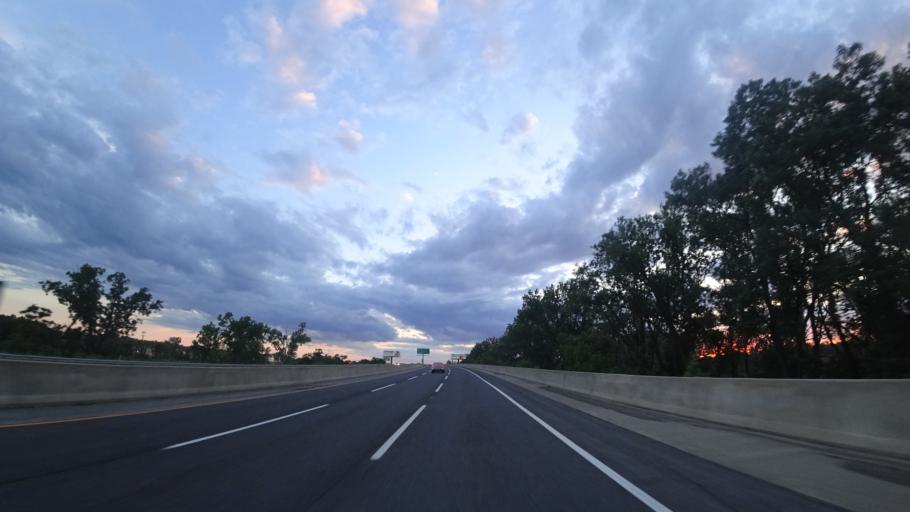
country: US
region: Indiana
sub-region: Lake County
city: Gary
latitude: 41.6097
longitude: -87.3819
